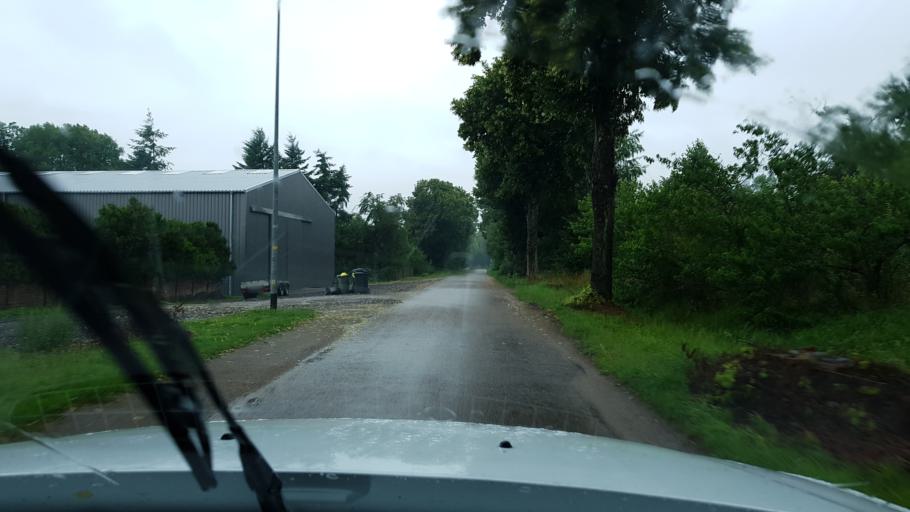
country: PL
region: West Pomeranian Voivodeship
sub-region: Powiat kolobrzeski
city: Ustronie Morskie
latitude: 54.2133
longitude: 15.8805
